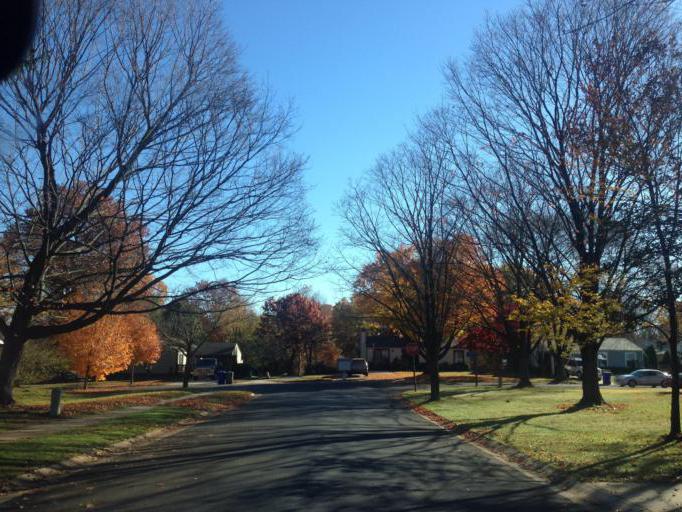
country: US
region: Maryland
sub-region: Howard County
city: Riverside
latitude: 39.1858
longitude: -76.8772
